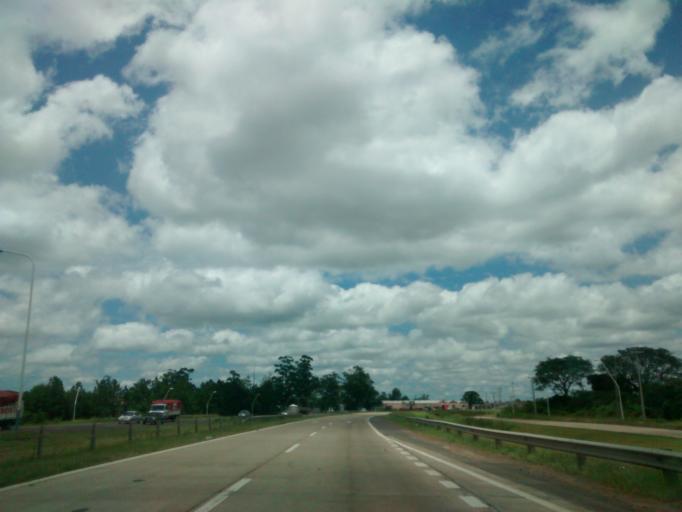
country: AR
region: Chaco
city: Fontana
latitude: -27.4113
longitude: -58.9930
